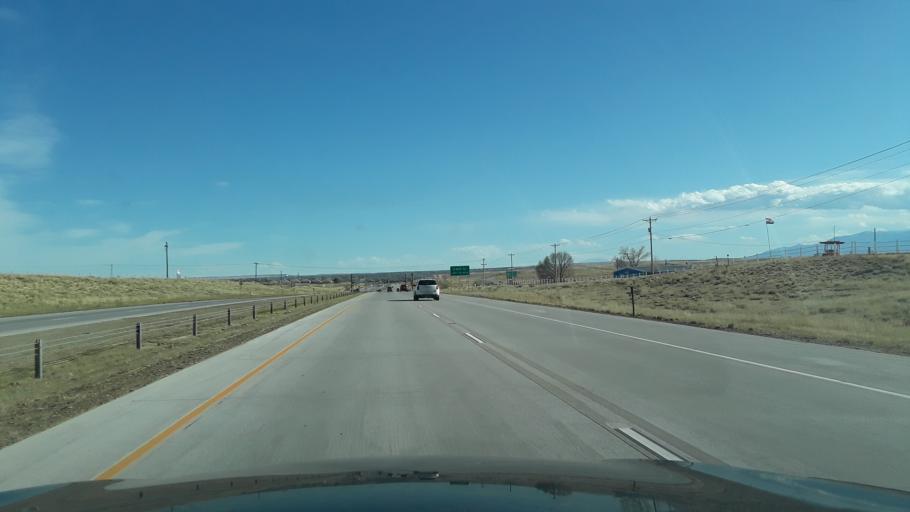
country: US
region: Colorado
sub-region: Pueblo County
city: Pueblo
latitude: 38.2971
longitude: -104.6636
